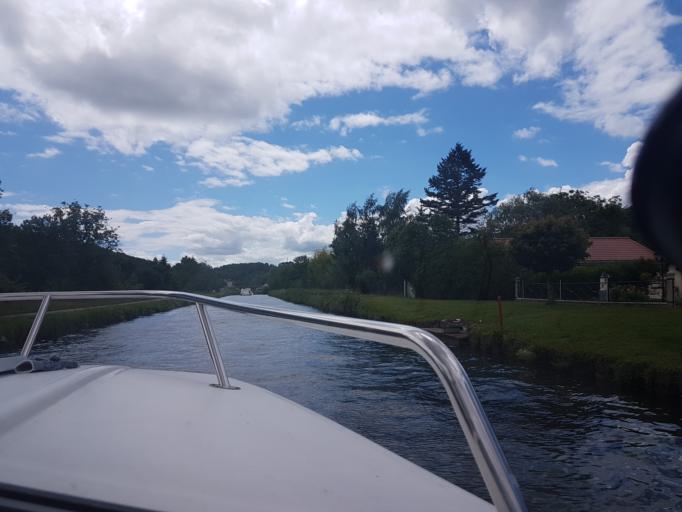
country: FR
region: Bourgogne
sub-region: Departement de l'Yonne
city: Vermenton
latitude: 47.6061
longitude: 3.6832
